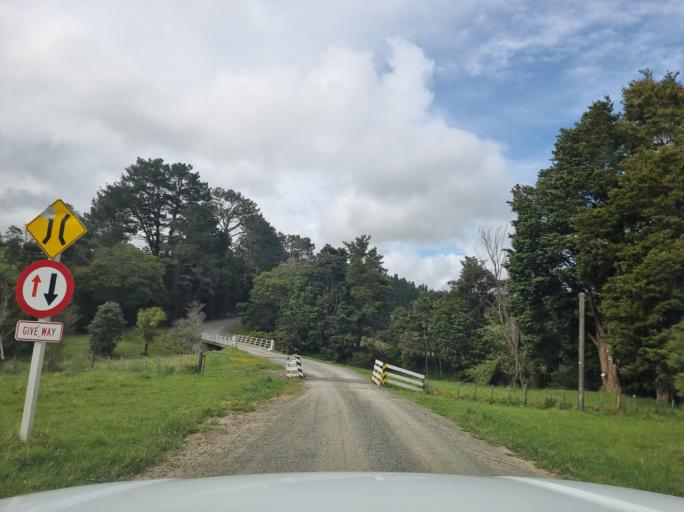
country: NZ
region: Northland
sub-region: Whangarei
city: Ruakaka
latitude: -36.1056
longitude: 174.2066
